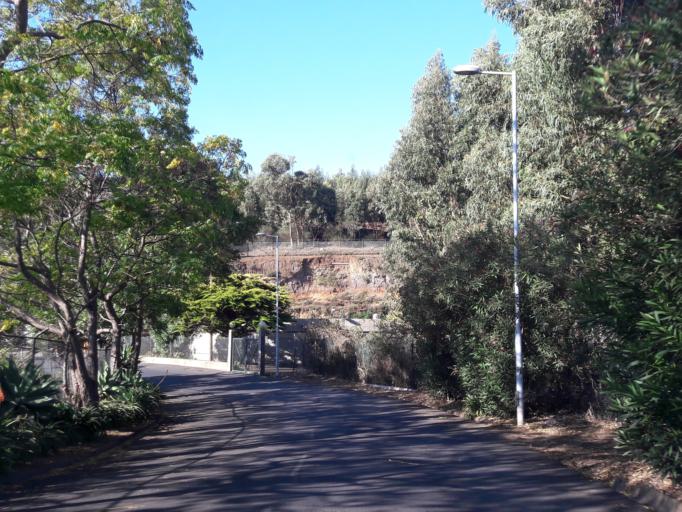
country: PT
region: Madeira
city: Canico
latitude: 32.6520
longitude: -16.8628
